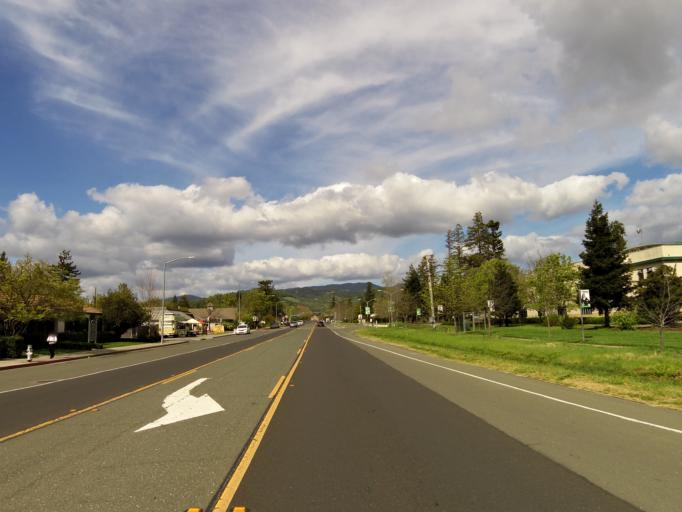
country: US
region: California
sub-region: Sonoma County
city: Sonoma
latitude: 38.2820
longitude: -122.4594
